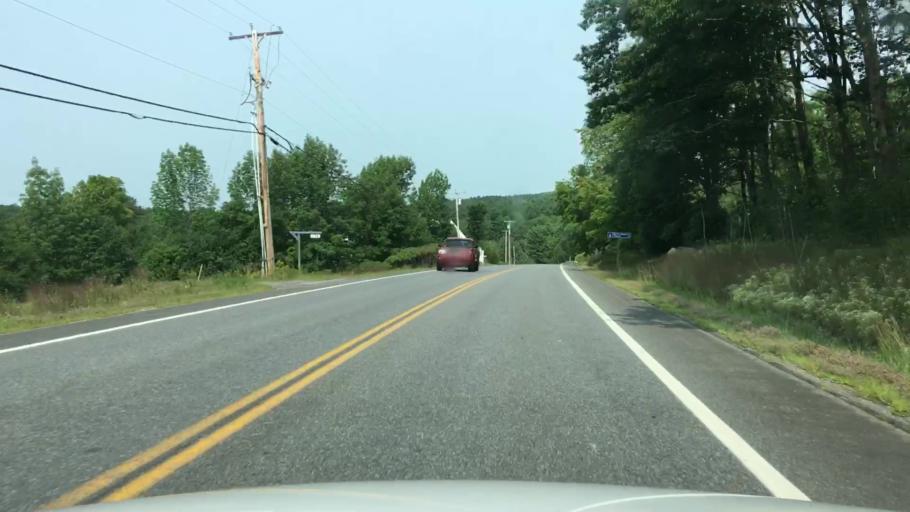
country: US
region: Maine
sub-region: Kennebec County
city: Winthrop
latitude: 44.3361
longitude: -70.0147
